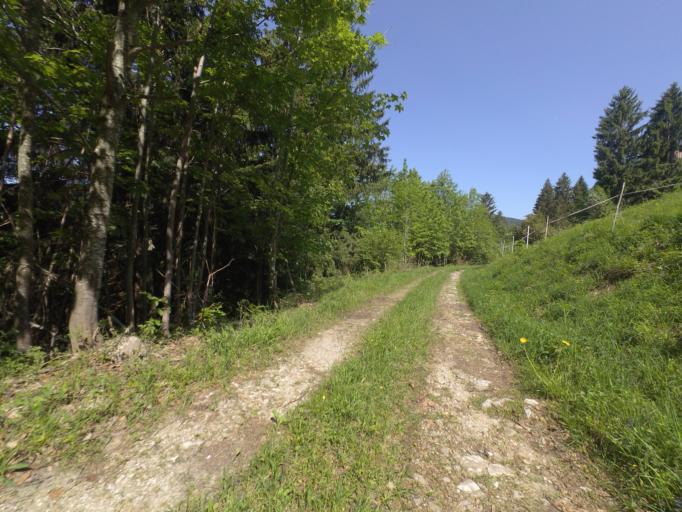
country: AT
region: Salzburg
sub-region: Politischer Bezirk Salzburg-Umgebung
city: Koppl
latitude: 47.7825
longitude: 13.1325
